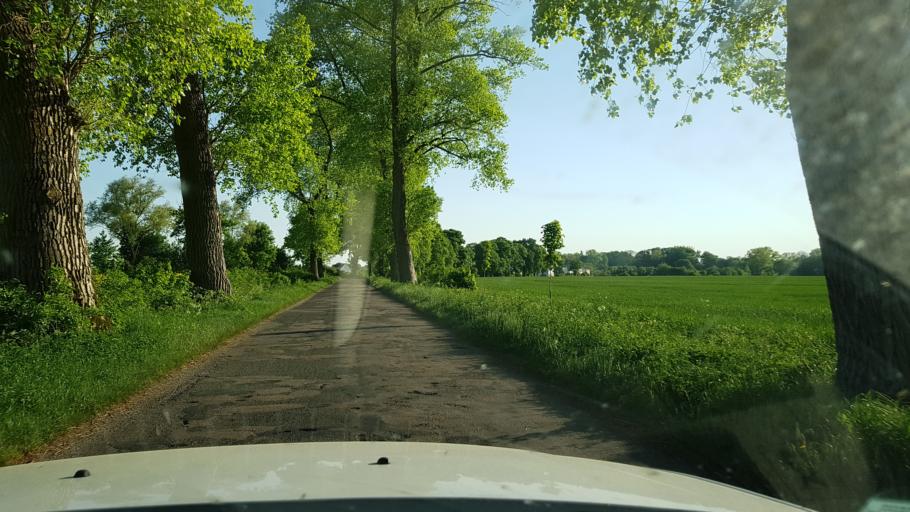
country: PL
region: West Pomeranian Voivodeship
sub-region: Powiat lobeski
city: Dobra
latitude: 53.5866
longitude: 15.3246
